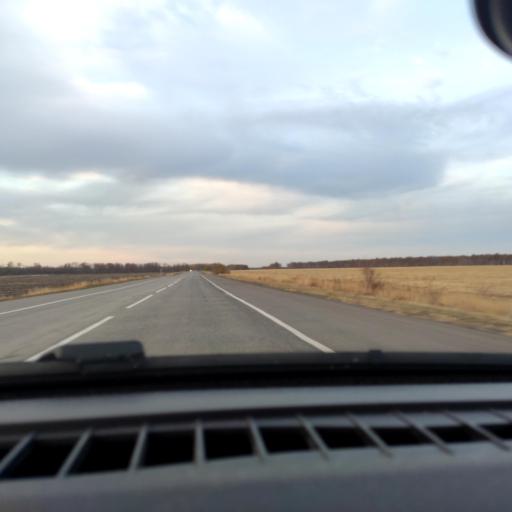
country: RU
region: Voronezj
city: Devitsa
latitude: 51.5812
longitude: 38.9758
